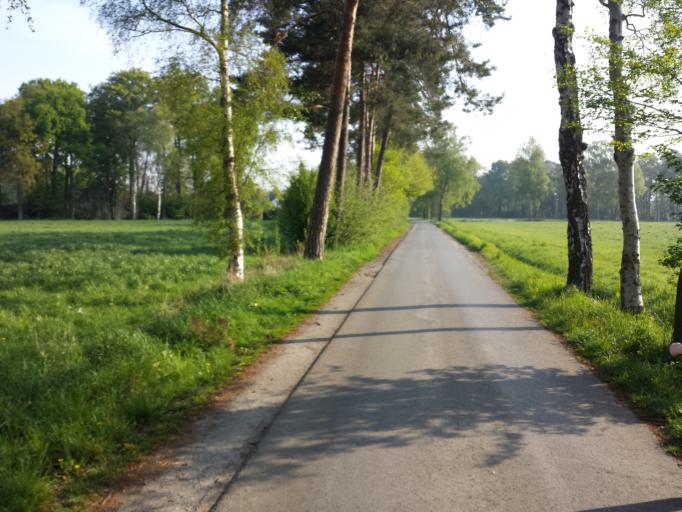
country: DE
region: North Rhine-Westphalia
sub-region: Regierungsbezirk Detmold
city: Guetersloh
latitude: 51.9153
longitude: 8.3386
